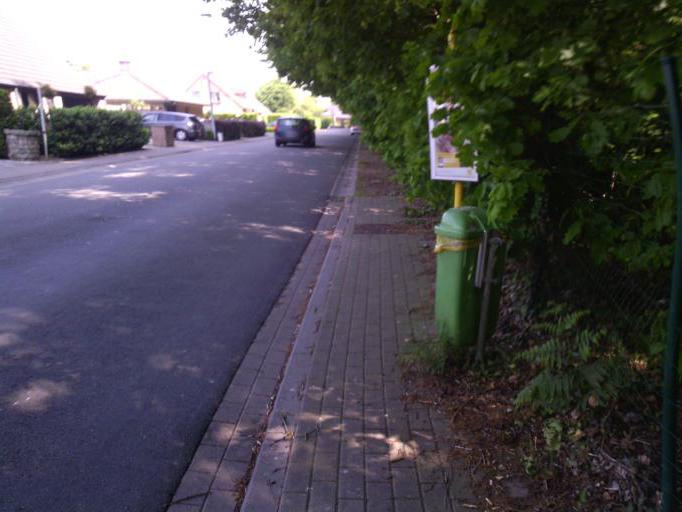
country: BE
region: Flanders
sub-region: Provincie West-Vlaanderen
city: Zedelgem
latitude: 51.1289
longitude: 3.1730
